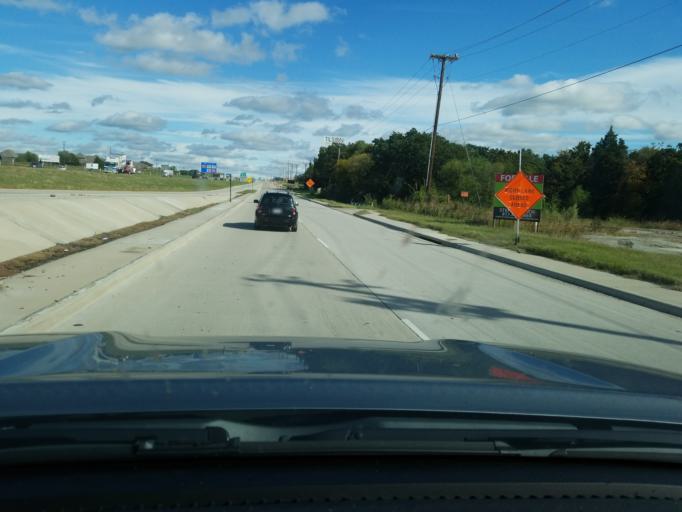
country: US
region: Texas
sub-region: Parker County
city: Weatherford
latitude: 32.7279
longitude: -97.8194
